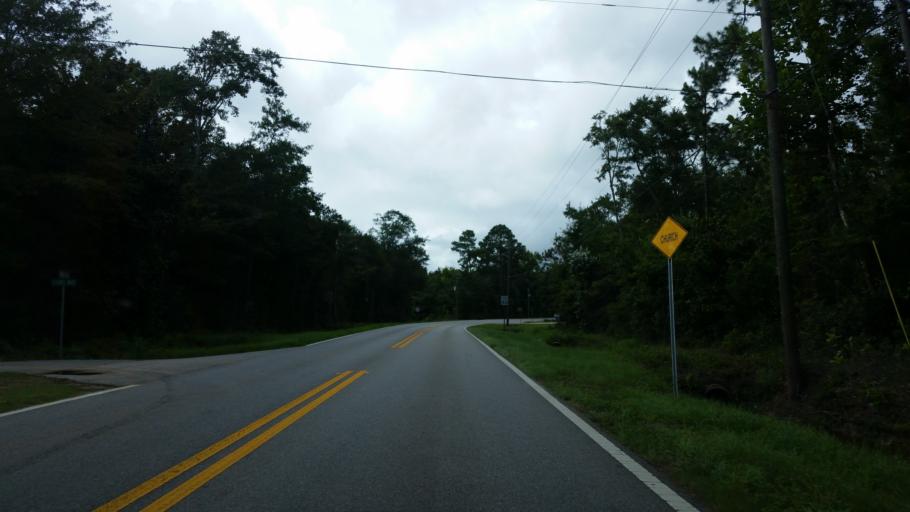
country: US
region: Florida
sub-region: Santa Rosa County
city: East Milton
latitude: 30.6097
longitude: -87.0203
